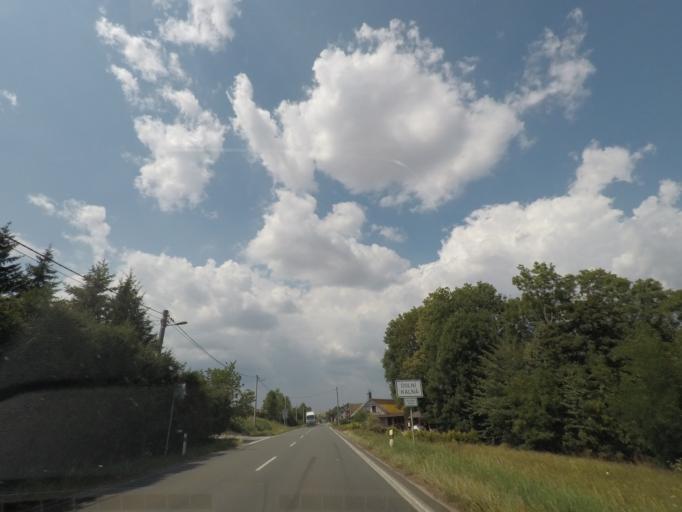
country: CZ
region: Kralovehradecky
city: Zadni Mostek
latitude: 50.5391
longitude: 15.6526
